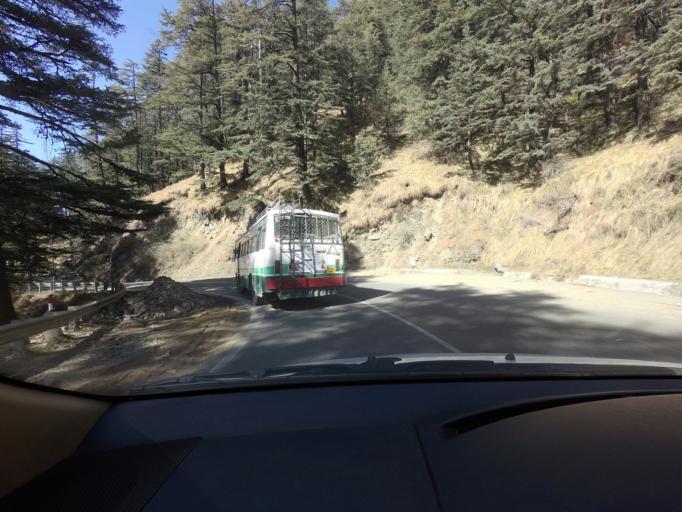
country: IN
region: Himachal Pradesh
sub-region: Shimla
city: Shimla
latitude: 31.1194
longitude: 77.2341
